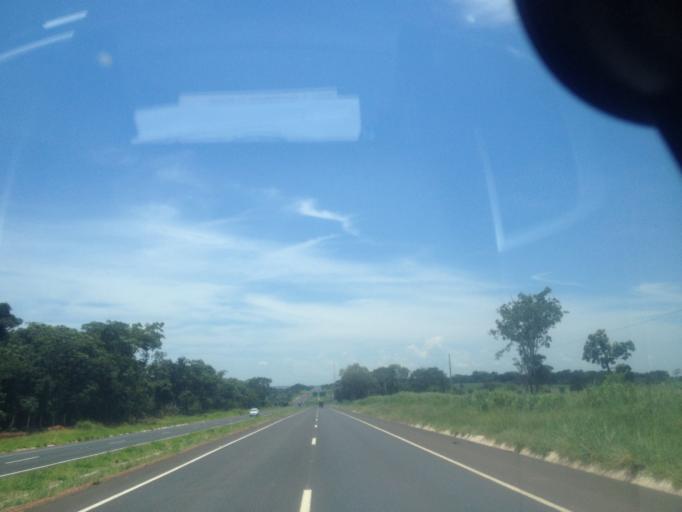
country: BR
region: Minas Gerais
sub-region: Monte Alegre De Minas
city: Monte Alegre de Minas
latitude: -18.8504
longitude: -48.8049
